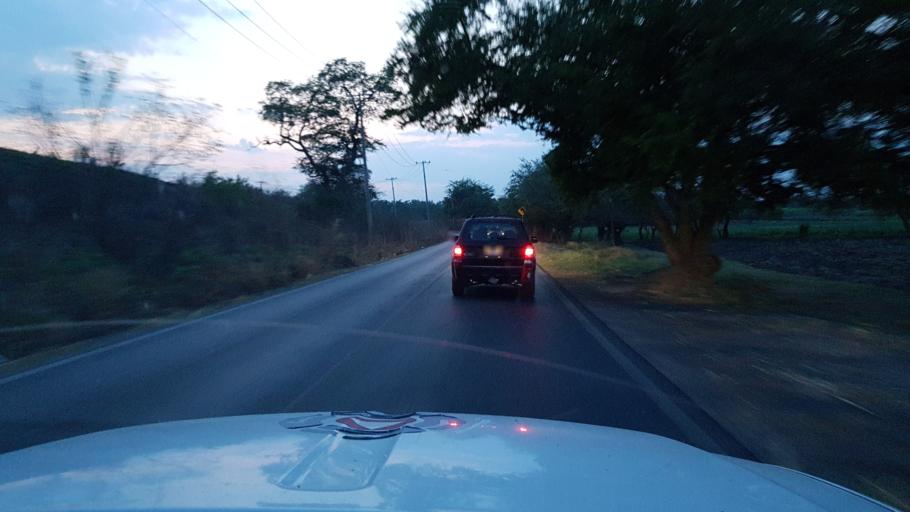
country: MX
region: Morelos
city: Tlaltizapan
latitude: 18.6898
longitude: -99.1432
